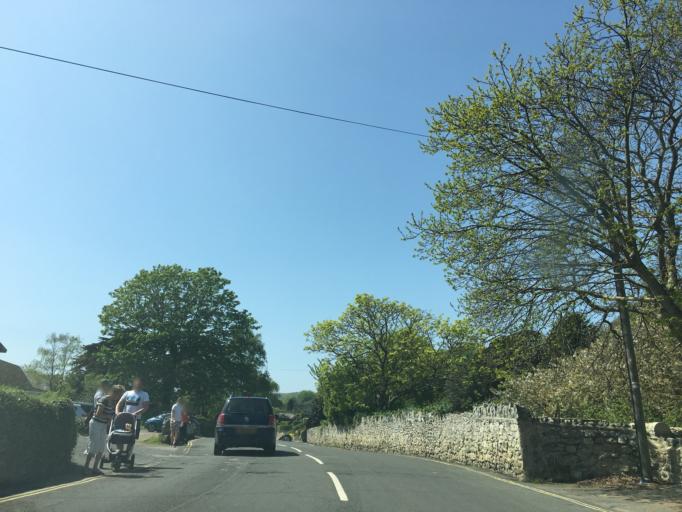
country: GB
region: England
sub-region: Isle of Wight
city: Ventnor
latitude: 50.5907
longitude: -1.2227
